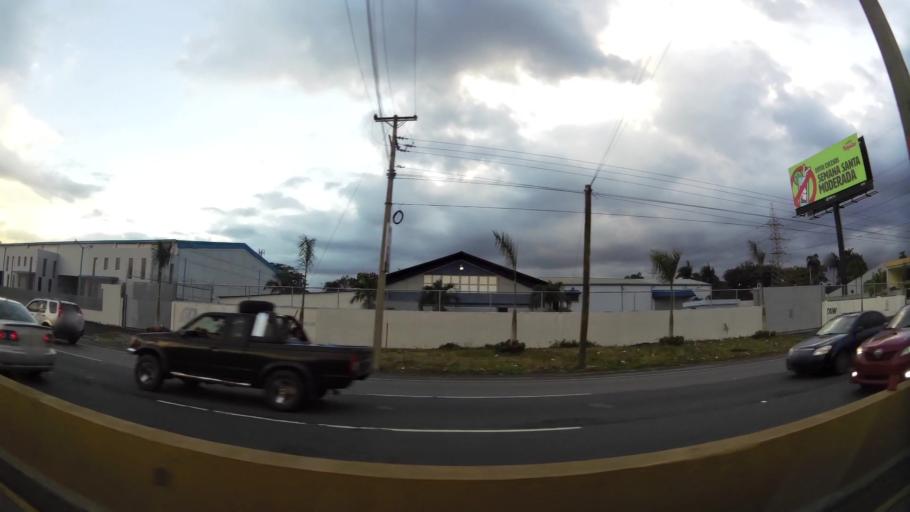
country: DO
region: Santo Domingo
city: Santo Domingo Oeste
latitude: 18.5536
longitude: -70.0556
